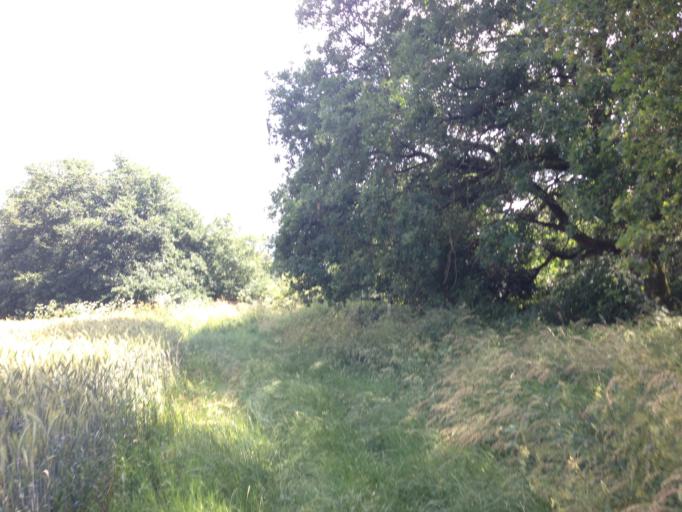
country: DE
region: Hesse
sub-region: Regierungsbezirk Giessen
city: Marburg an der Lahn
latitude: 50.8514
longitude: 8.7501
